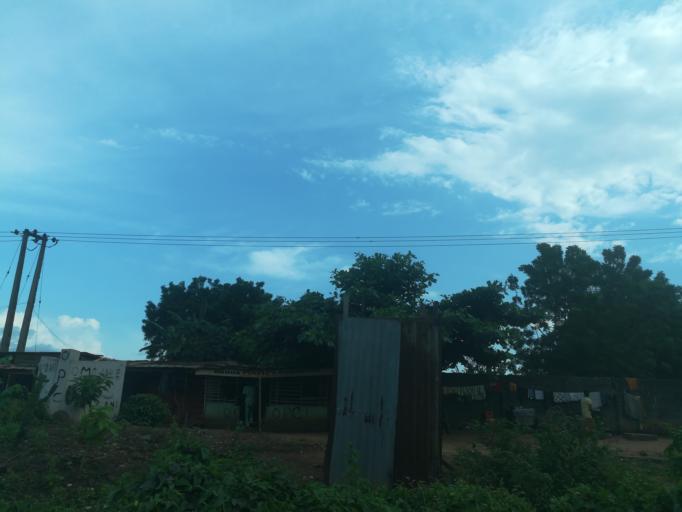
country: NG
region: Lagos
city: Ikorodu
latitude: 6.6260
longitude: 3.5008
